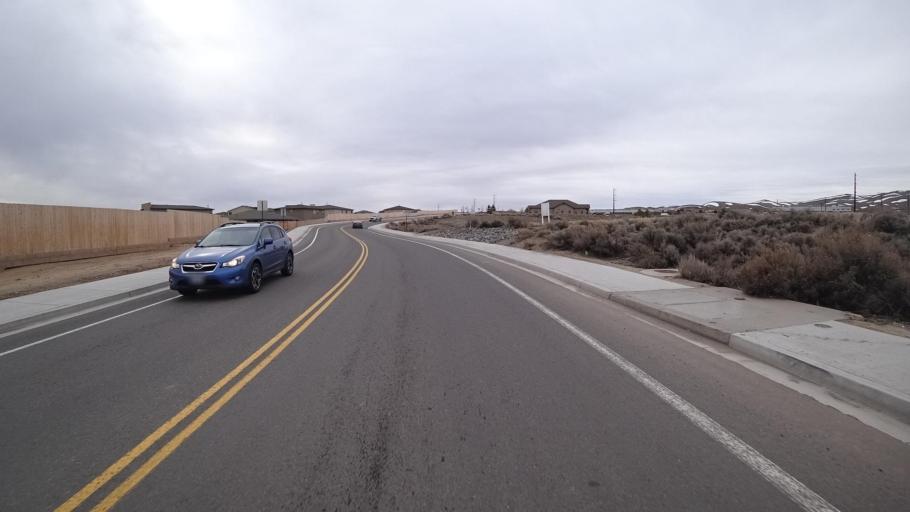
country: US
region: Nevada
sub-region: Washoe County
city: Golden Valley
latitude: 39.6133
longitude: -119.8454
